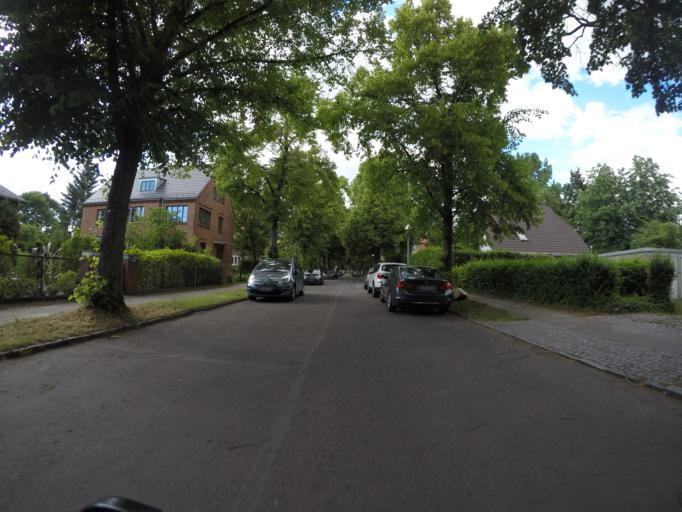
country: DE
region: Berlin
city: Zehlendorf Bezirk
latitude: 52.4254
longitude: 13.2663
